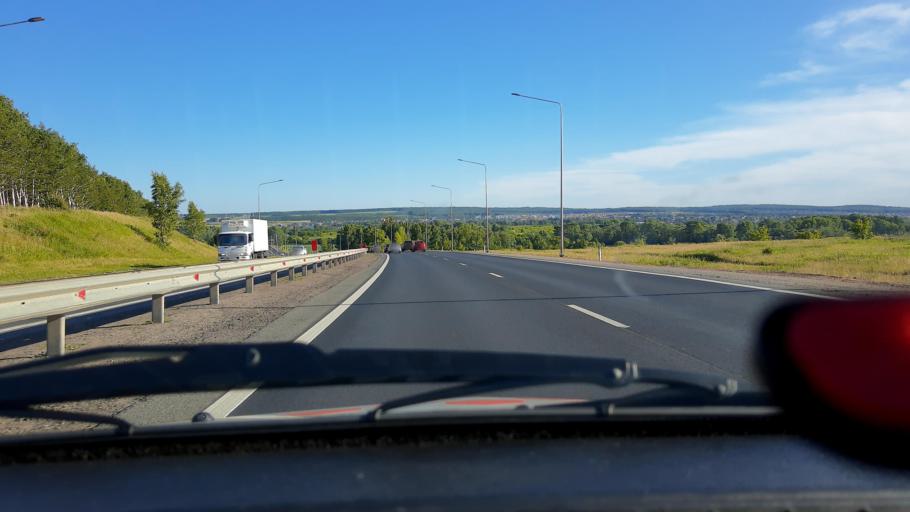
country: RU
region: Bashkortostan
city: Avdon
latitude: 54.5220
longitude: 55.8969
